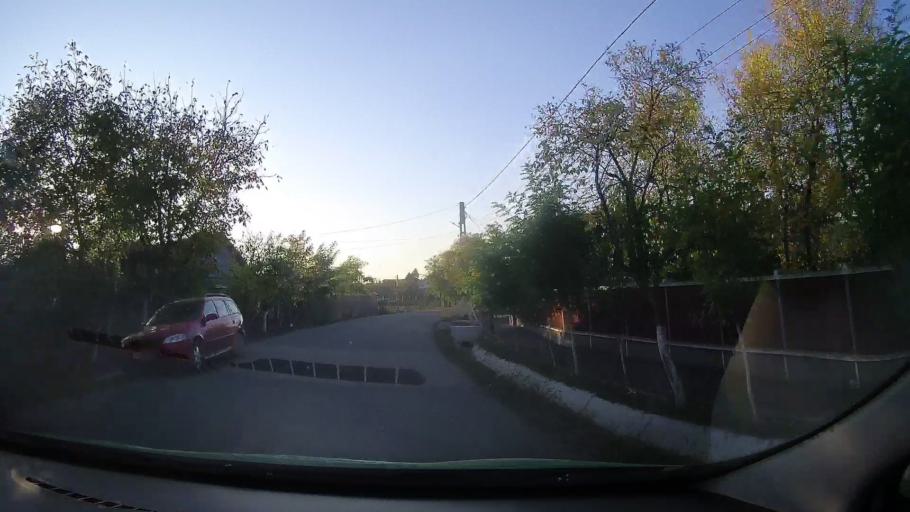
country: RO
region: Bihor
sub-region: Comuna Salard
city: Salard
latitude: 47.2233
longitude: 22.0334
